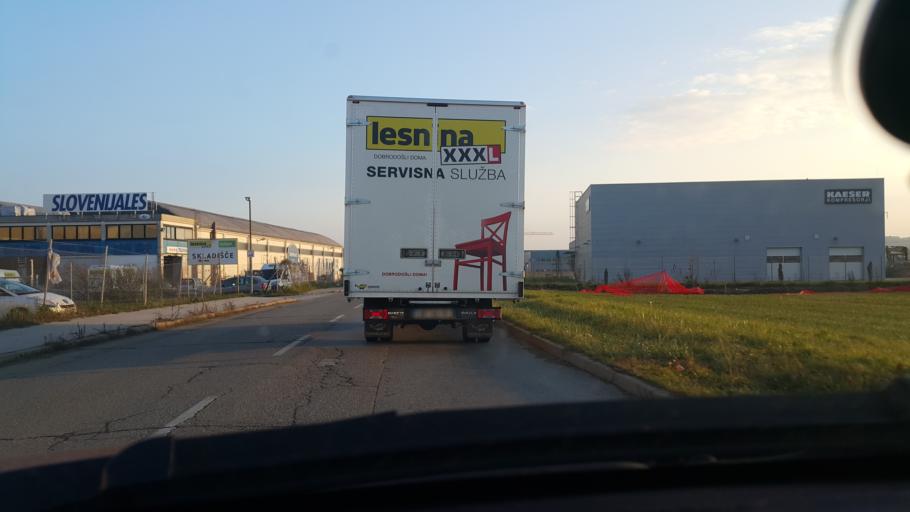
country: SI
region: Hoce-Slivnica
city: Spodnje Hoce
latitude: 46.4993
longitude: 15.6568
